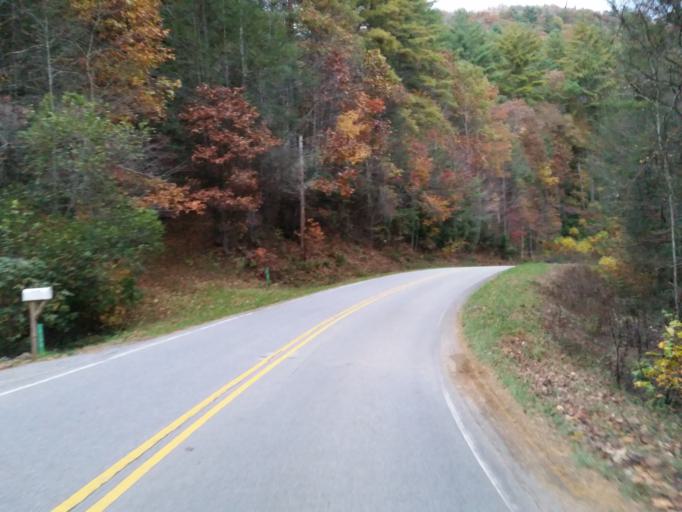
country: US
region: Georgia
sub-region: Union County
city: Blairsville
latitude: 34.7391
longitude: -84.0893
